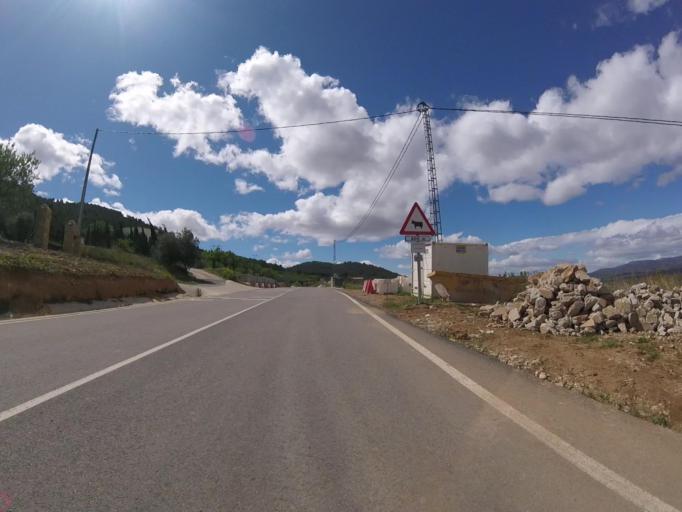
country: ES
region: Valencia
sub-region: Provincia de Castello
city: Culla
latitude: 40.2820
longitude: -0.1121
